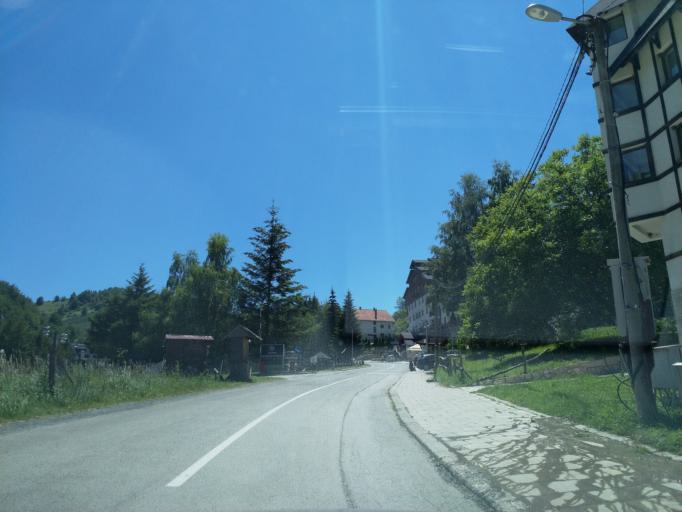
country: XK
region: Mitrovica
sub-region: Komuna e Leposaviqit
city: Leposaviq
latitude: 43.2879
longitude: 20.8798
